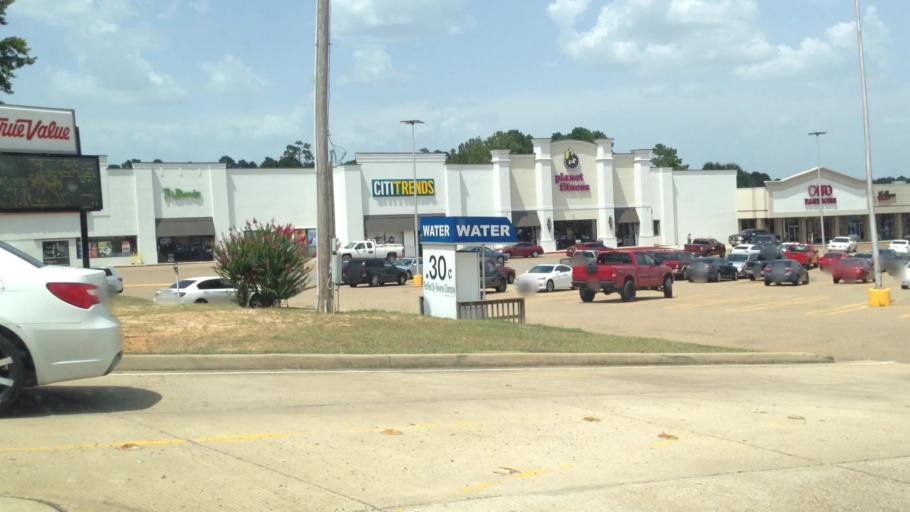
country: US
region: Louisiana
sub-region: Lincoln Parish
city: Ruston
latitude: 32.5418
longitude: -92.6380
